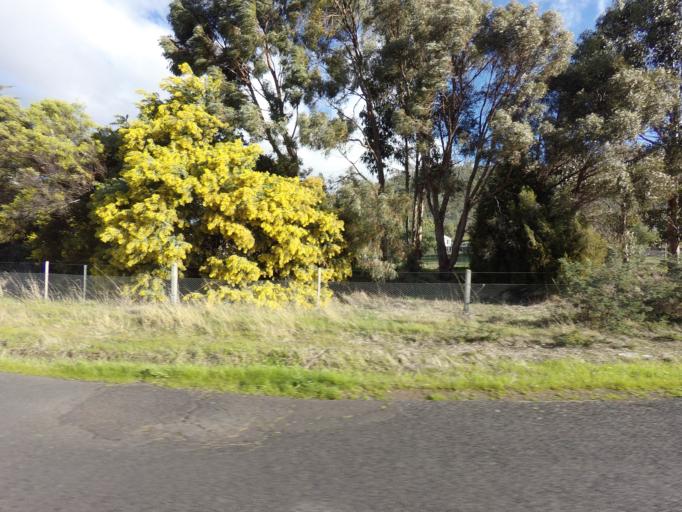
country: AU
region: Tasmania
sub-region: Derwent Valley
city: New Norfolk
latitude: -42.7484
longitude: 147.0453
